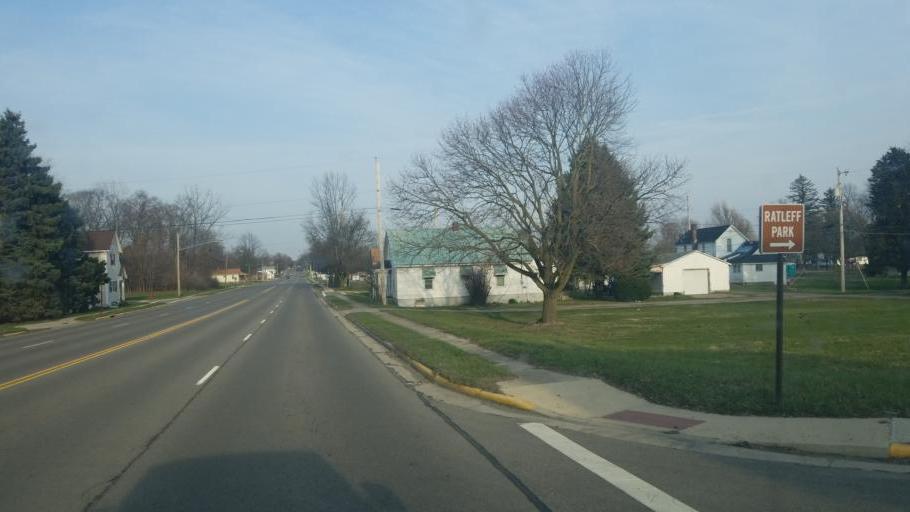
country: US
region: Ohio
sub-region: Logan County
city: Bellefontaine
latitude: 40.3635
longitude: -83.7753
